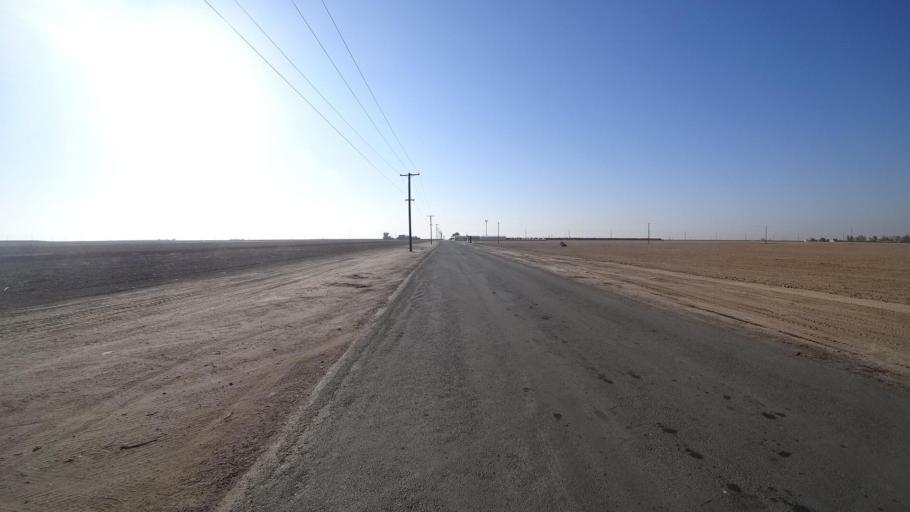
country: US
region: California
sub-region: Tulare County
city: Richgrove
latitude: 35.7812
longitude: -119.1607
